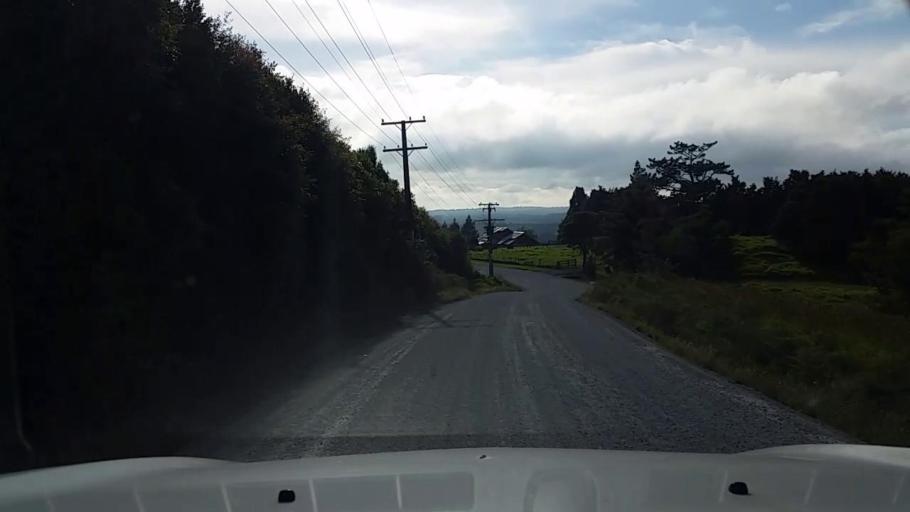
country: NZ
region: Northland
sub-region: Whangarei
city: Maungatapere
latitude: -35.6832
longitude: 174.1812
